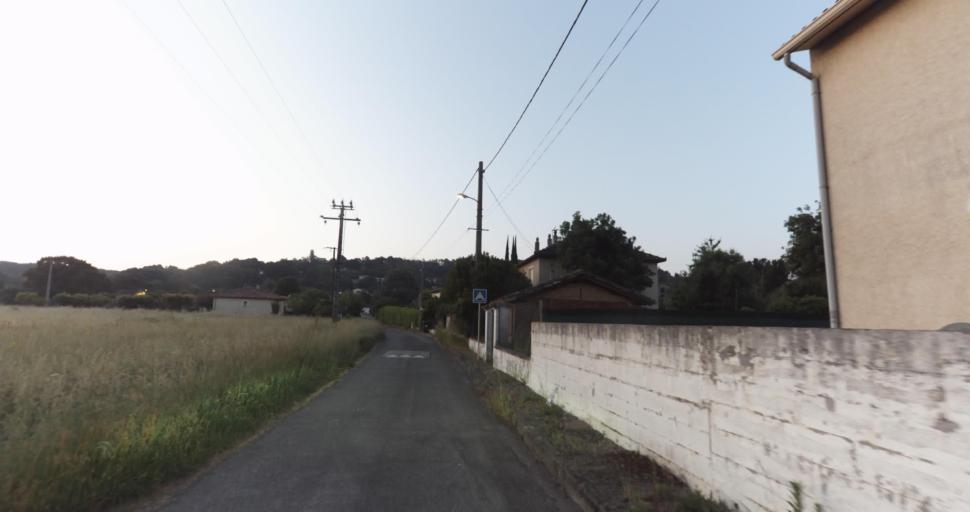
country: FR
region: Midi-Pyrenees
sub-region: Departement de la Haute-Garonne
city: Levignac
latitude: 43.6690
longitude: 1.1942
